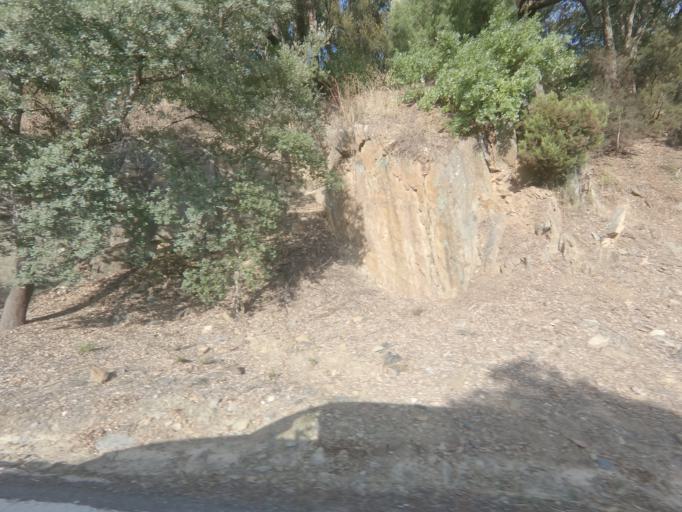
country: PT
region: Vila Real
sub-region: Sabrosa
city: Vilela
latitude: 41.2101
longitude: -7.5406
